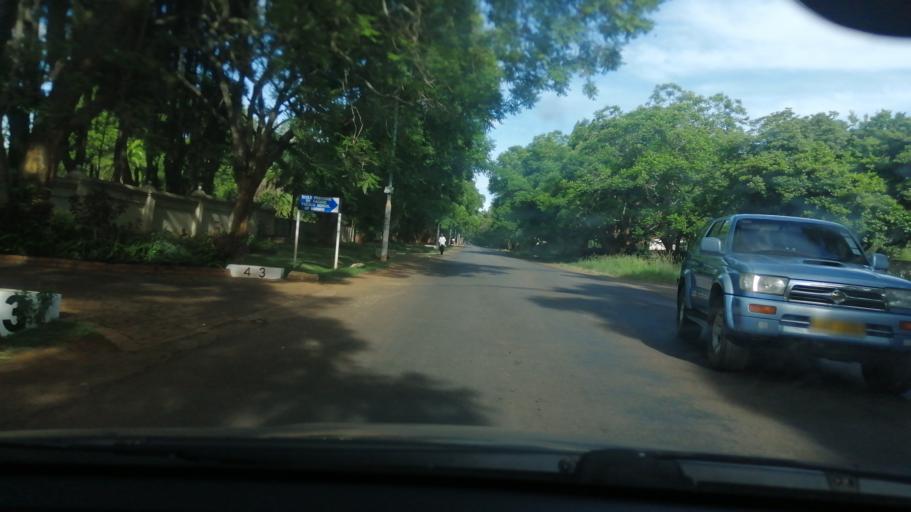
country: ZW
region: Harare
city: Harare
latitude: -17.7628
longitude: 31.0738
